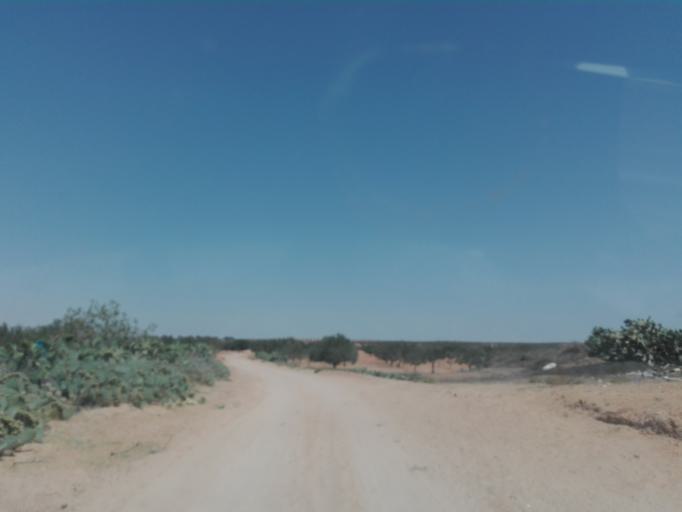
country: TN
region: Safaqis
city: Bi'r `Ali Bin Khalifah
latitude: 34.6469
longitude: 10.2592
